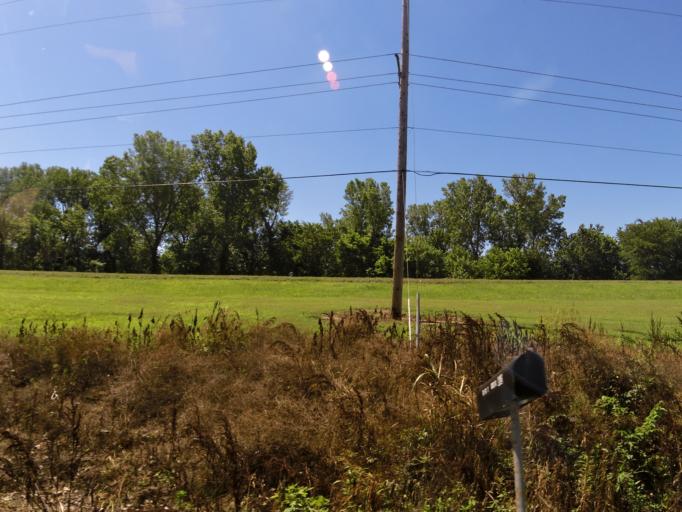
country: US
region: Missouri
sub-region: New Madrid County
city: New Madrid
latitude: 36.5833
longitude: -89.5451
